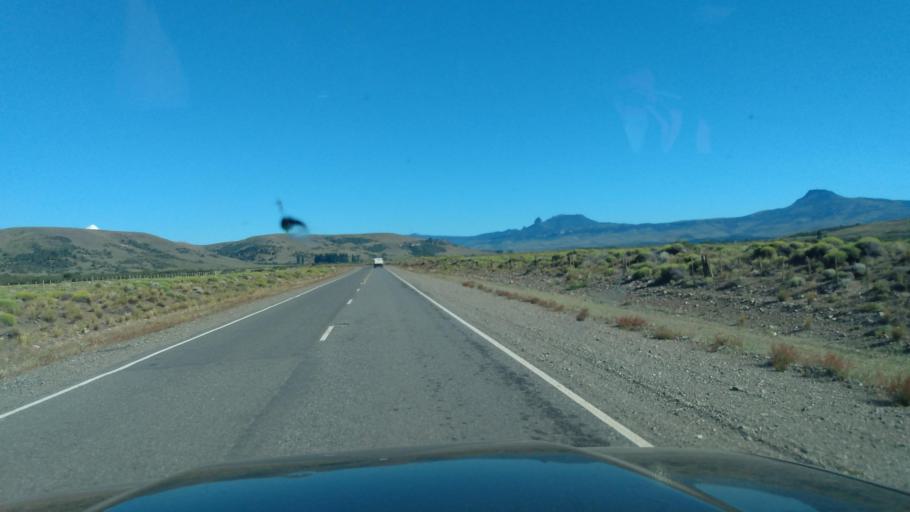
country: AR
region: Neuquen
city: Junin de los Andes
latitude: -39.8691
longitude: -71.1769
